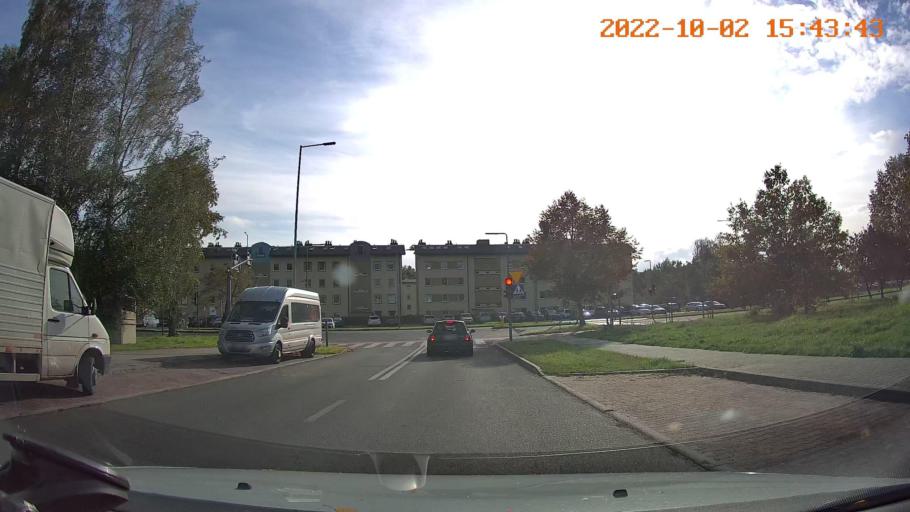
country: PL
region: Silesian Voivodeship
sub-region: Tychy
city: Tychy
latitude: 50.1031
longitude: 18.9826
